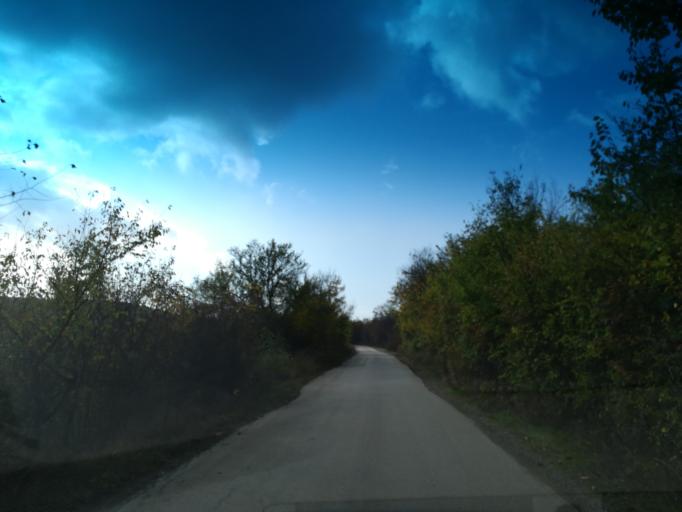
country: BG
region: Stara Zagora
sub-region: Obshtina Nikolaevo
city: Elkhovo
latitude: 42.3349
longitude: 25.4052
